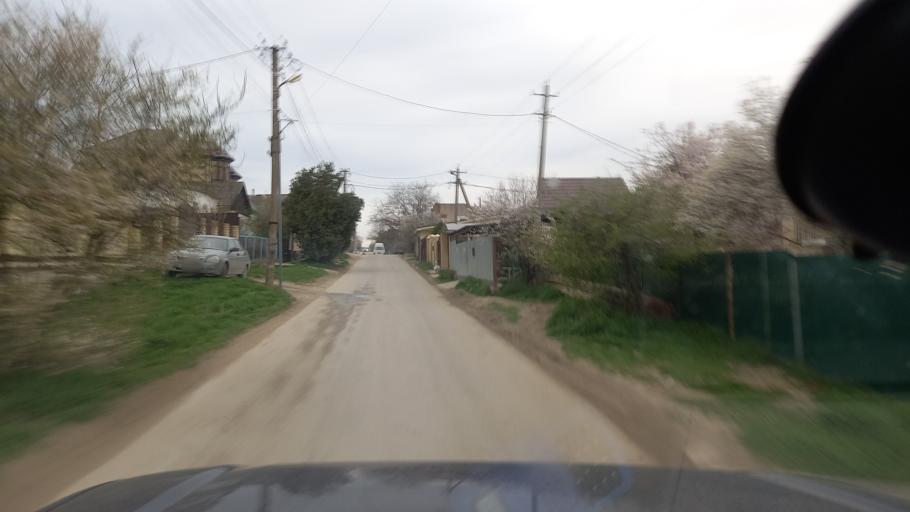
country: RU
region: Krasnodarskiy
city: Anapa
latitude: 44.8502
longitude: 37.3584
